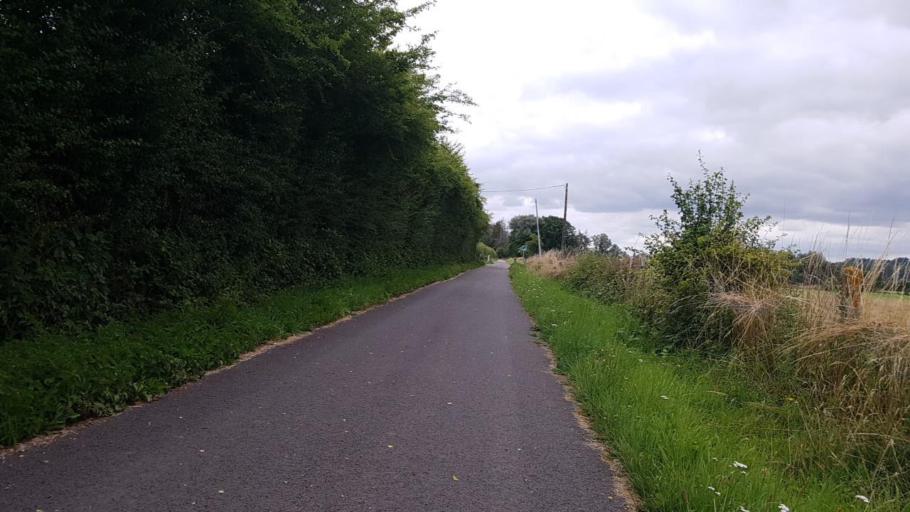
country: FR
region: Picardie
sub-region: Departement de l'Aisne
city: La Capelle
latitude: 49.9068
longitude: 3.9000
